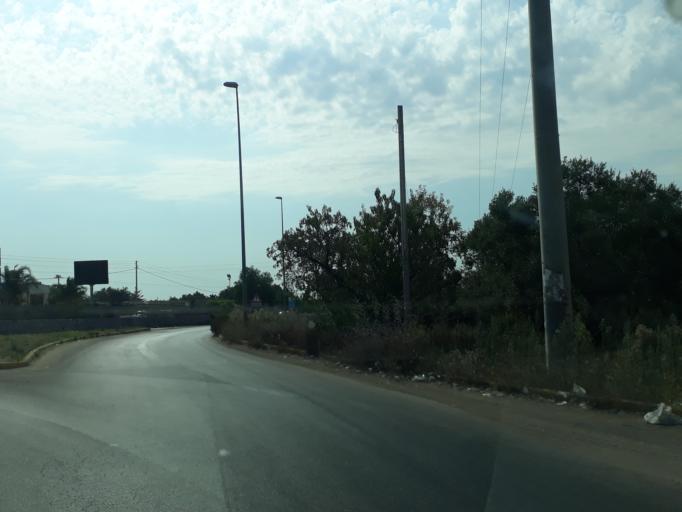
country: IT
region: Apulia
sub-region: Provincia di Brindisi
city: Carovigno
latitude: 40.6953
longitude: 17.6686
